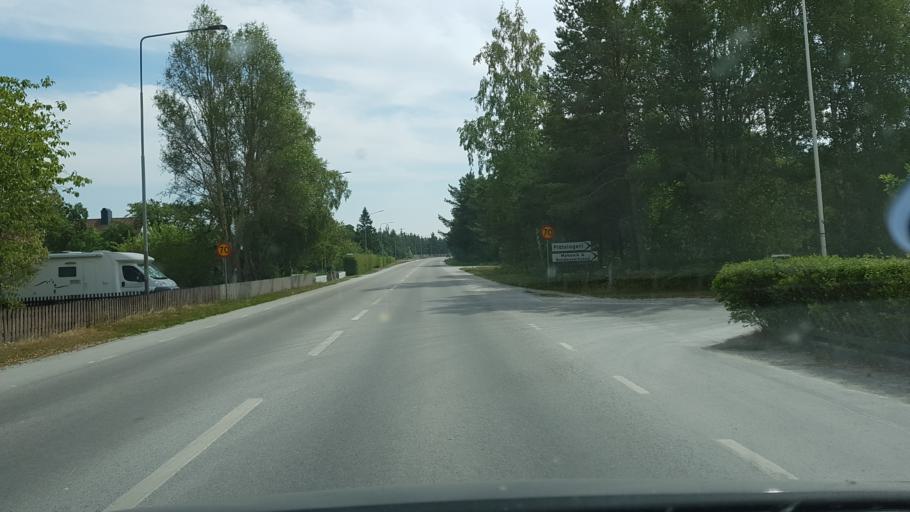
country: SE
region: Gotland
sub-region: Gotland
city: Slite
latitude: 57.7179
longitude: 18.7918
